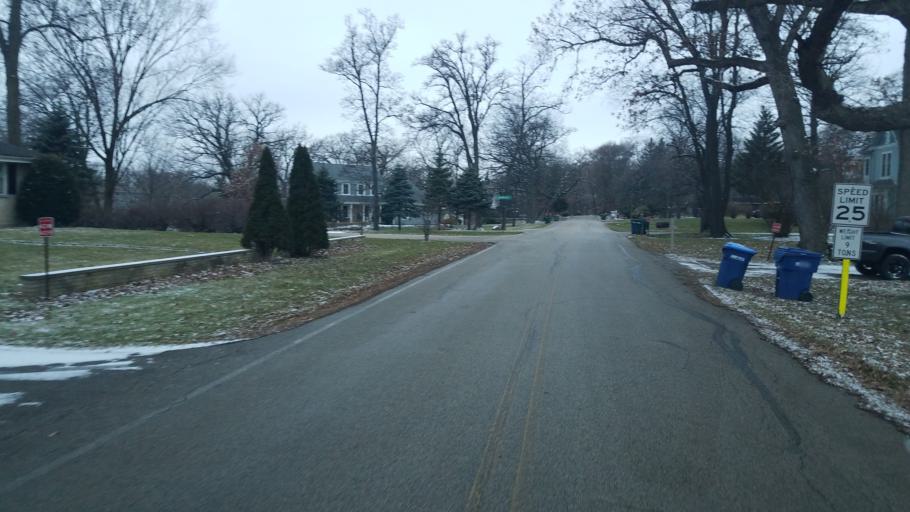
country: US
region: Illinois
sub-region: Kane County
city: Sugar Grove
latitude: 41.8103
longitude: -88.4615
